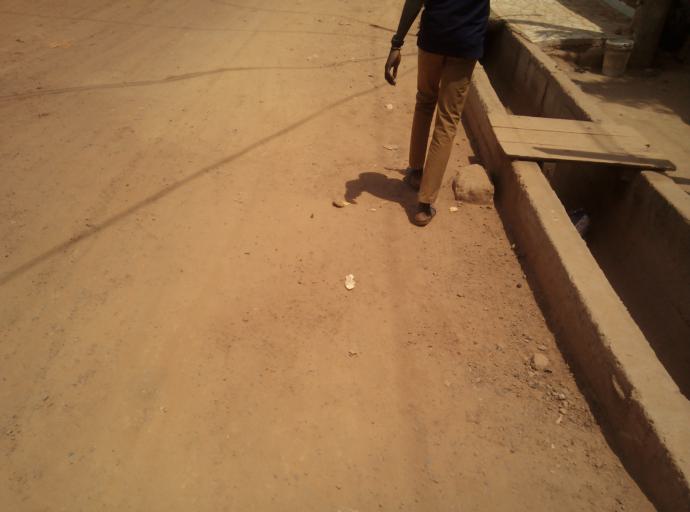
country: GH
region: Central
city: Cape Coast
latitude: 5.1346
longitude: -1.2930
